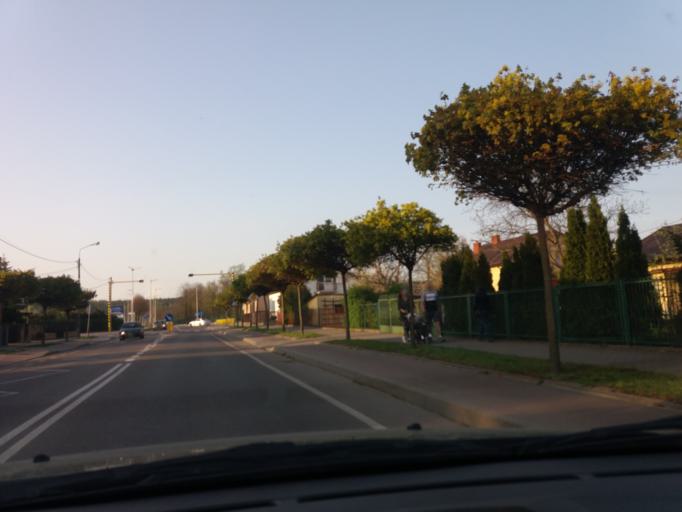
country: PL
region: Masovian Voivodeship
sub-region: Powiat mlawski
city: Mlawa
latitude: 53.1224
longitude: 20.3776
